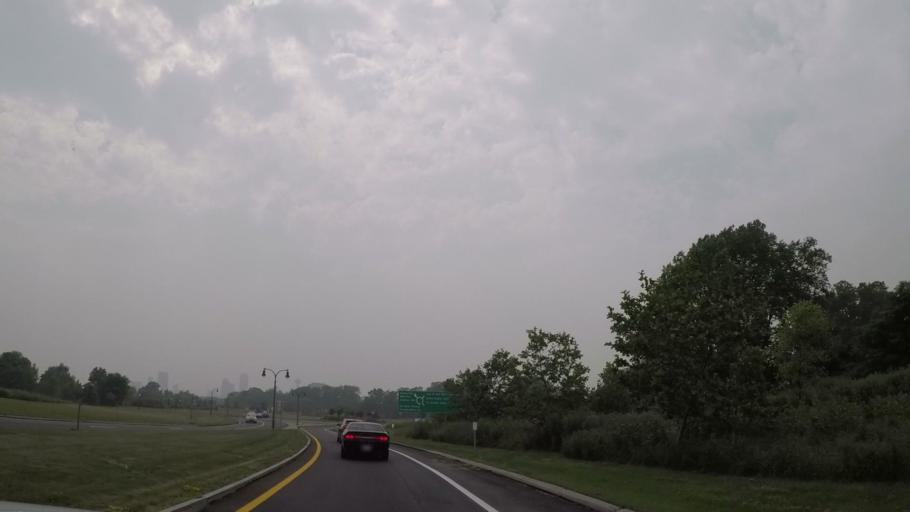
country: US
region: New York
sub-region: Niagara County
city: Niagara Falls
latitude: 43.0806
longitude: -79.0494
